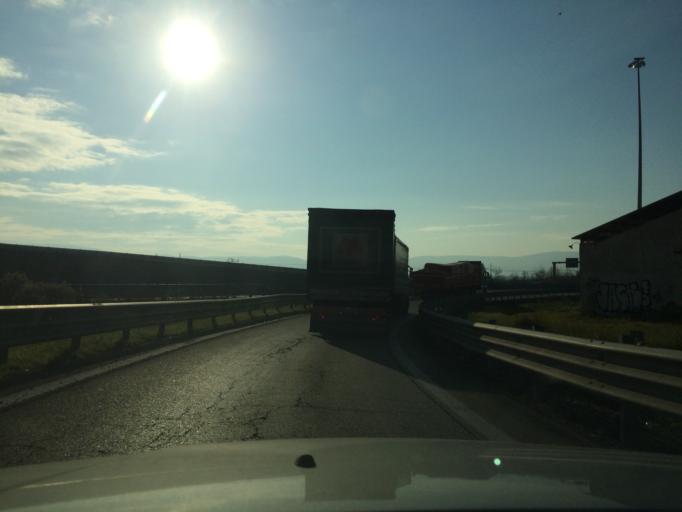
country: IT
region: Umbria
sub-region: Provincia di Terni
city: San Gemini
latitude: 42.5695
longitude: 12.5749
